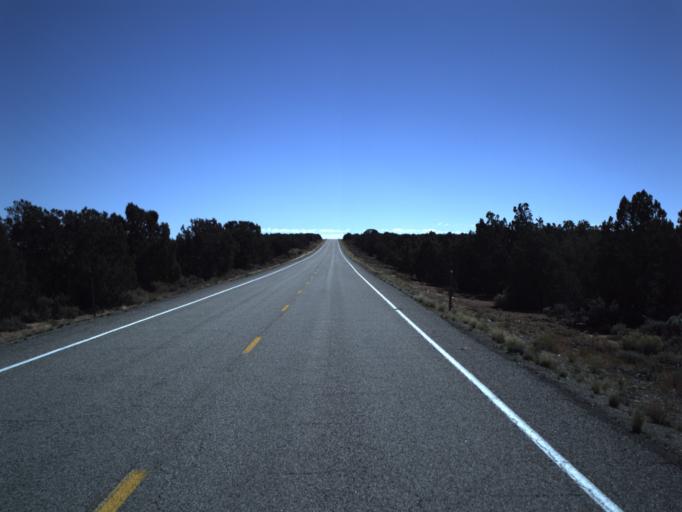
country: US
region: Utah
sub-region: San Juan County
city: Blanding
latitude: 37.5527
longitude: -109.9946
